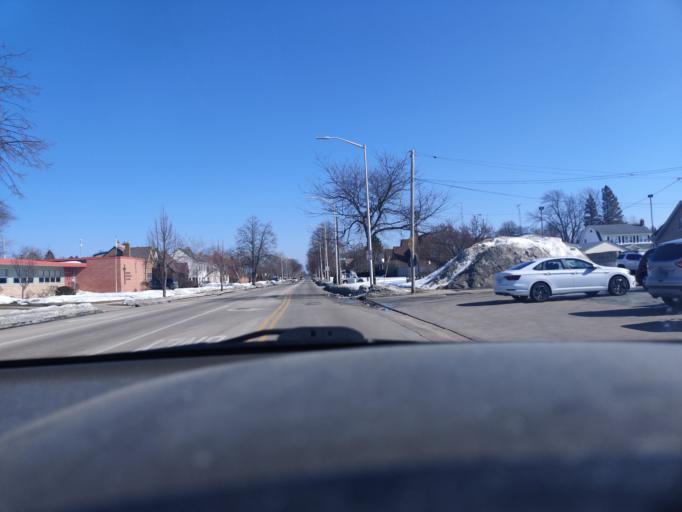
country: US
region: Wisconsin
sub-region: Kenosha County
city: Kenosha
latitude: 42.5659
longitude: -87.8351
